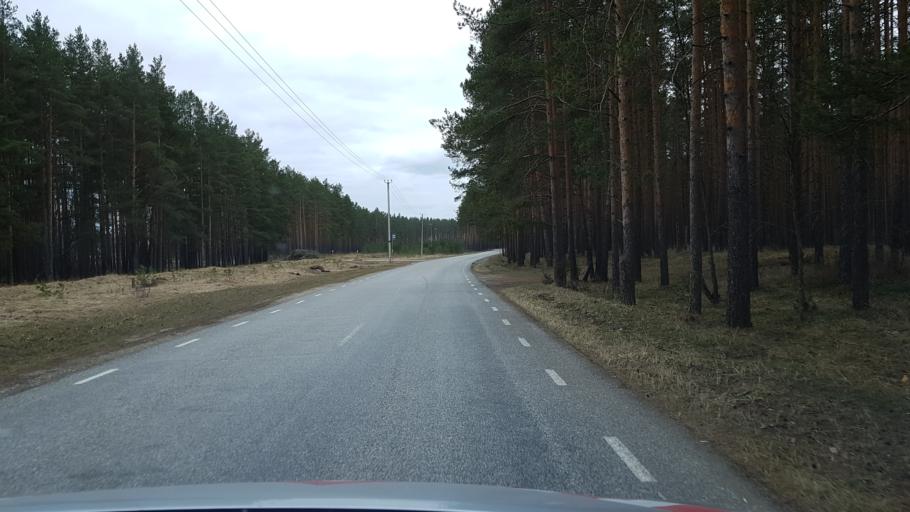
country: EE
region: Ida-Virumaa
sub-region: Narva-Joesuu linn
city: Narva-Joesuu
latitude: 59.4254
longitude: 28.1189
